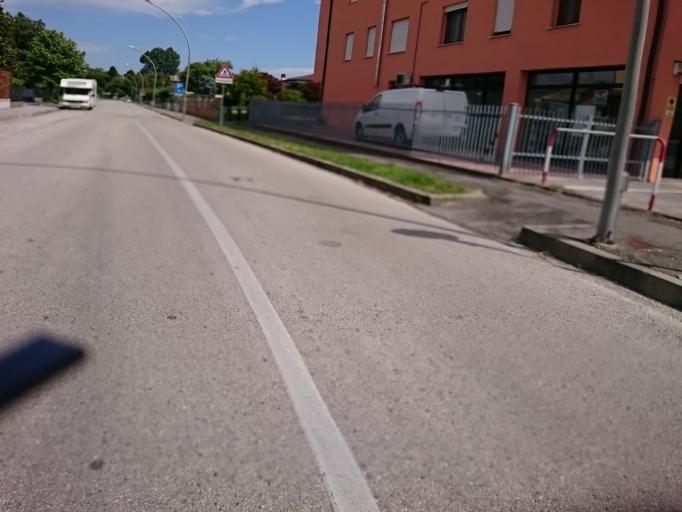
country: IT
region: Veneto
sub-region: Provincia di Padova
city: Caselle
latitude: 45.4162
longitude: 11.8092
